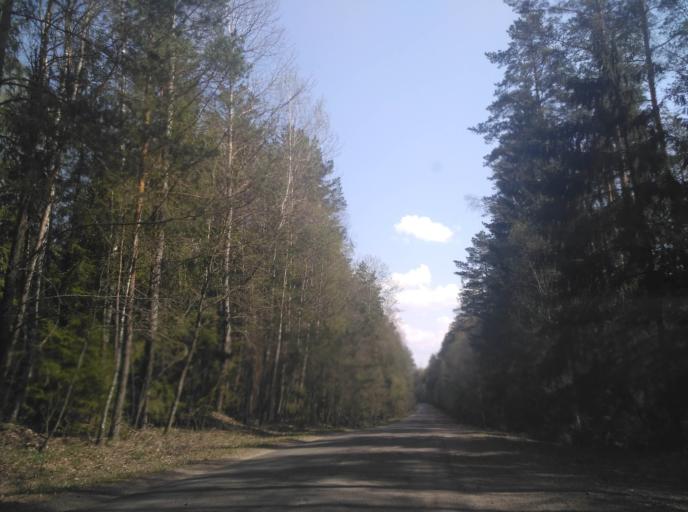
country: BY
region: Minsk
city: Loshnitsa
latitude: 54.4936
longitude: 28.7006
